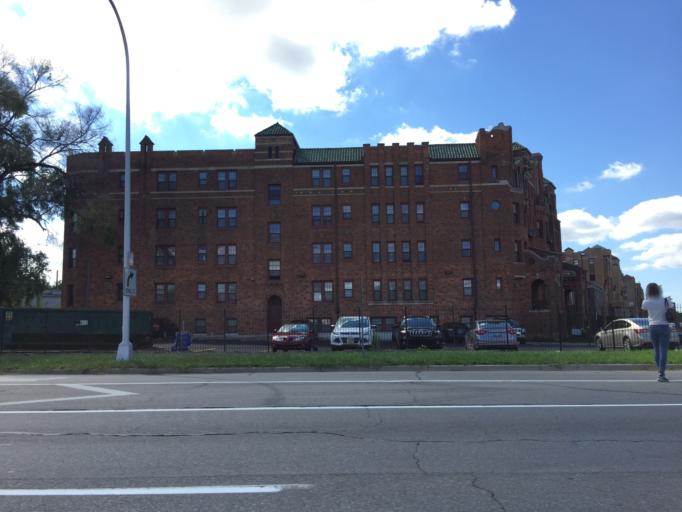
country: US
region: Michigan
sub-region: Wayne County
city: Highland Park
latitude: 42.4183
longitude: -83.1058
